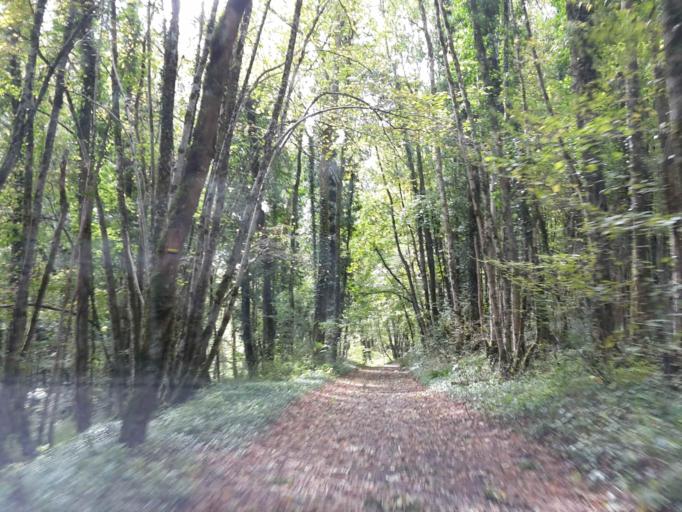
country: FR
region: Franche-Comte
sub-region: Departement du Doubs
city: Roulans
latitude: 47.2933
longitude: 6.2379
